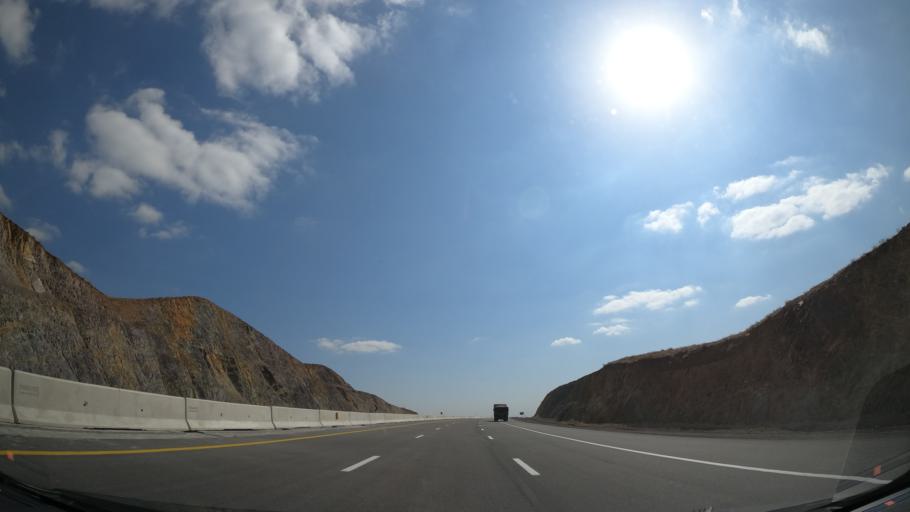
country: IR
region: Alborz
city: Nazarabad
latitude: 35.6811
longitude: 50.6423
